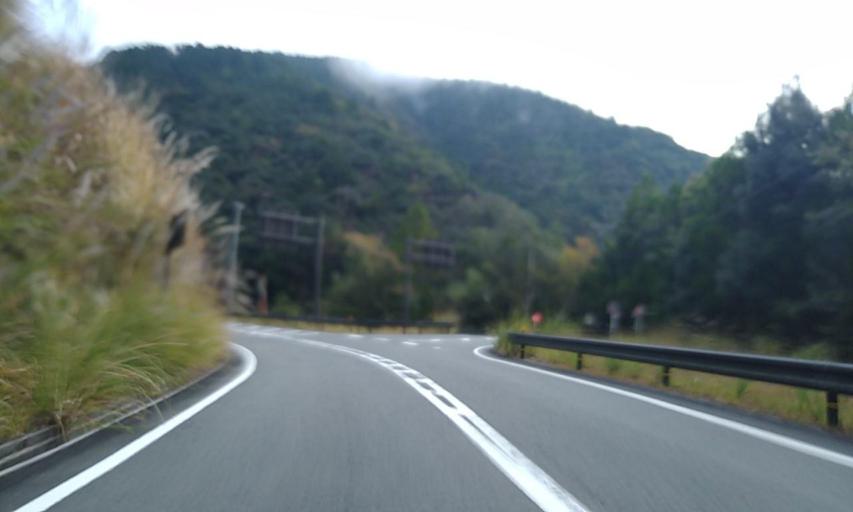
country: JP
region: Wakayama
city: Shingu
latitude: 33.8770
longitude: 135.8756
